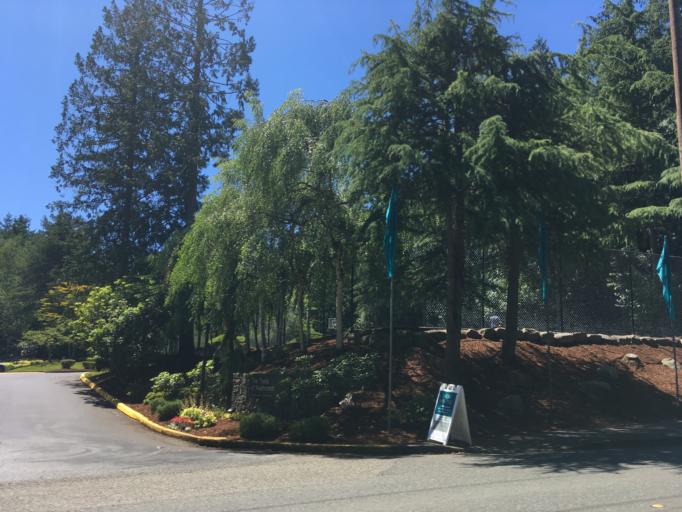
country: US
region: Washington
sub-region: King County
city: Redmond
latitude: 47.6461
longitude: -122.1165
